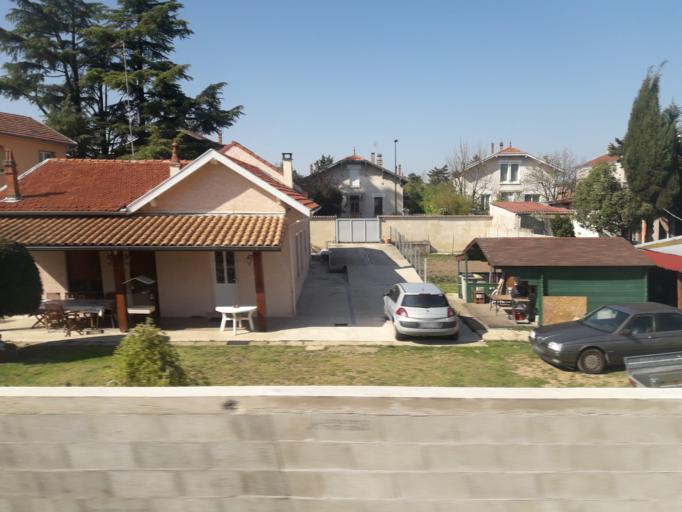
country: FR
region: Rhone-Alpes
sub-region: Departement de la Drome
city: Romans-sur-Isere
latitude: 45.0484
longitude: 5.0646
